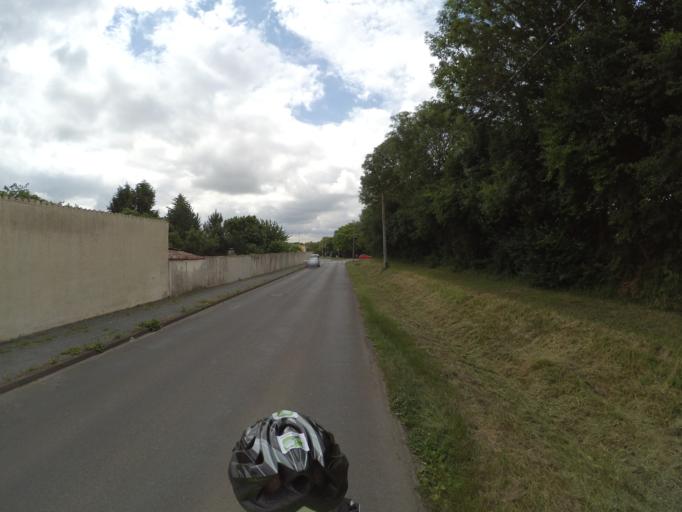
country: FR
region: Poitou-Charentes
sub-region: Departement de la Charente-Maritime
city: Breuil-Magne
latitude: 45.9591
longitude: -0.9695
